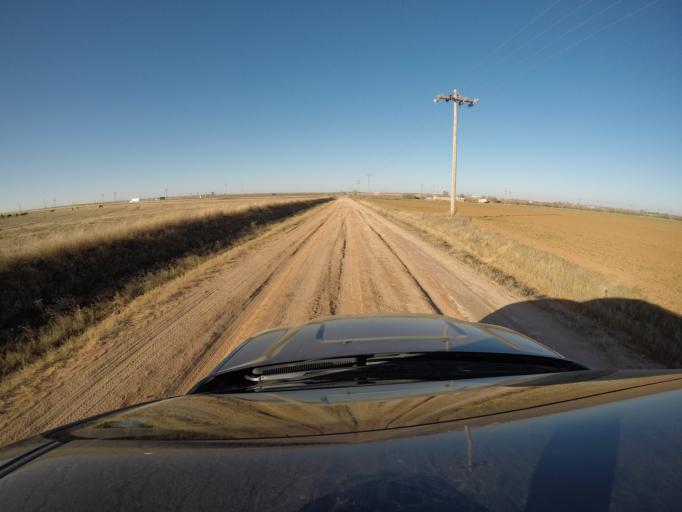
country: US
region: New Mexico
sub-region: Curry County
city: Texico
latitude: 34.3884
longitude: -103.1082
